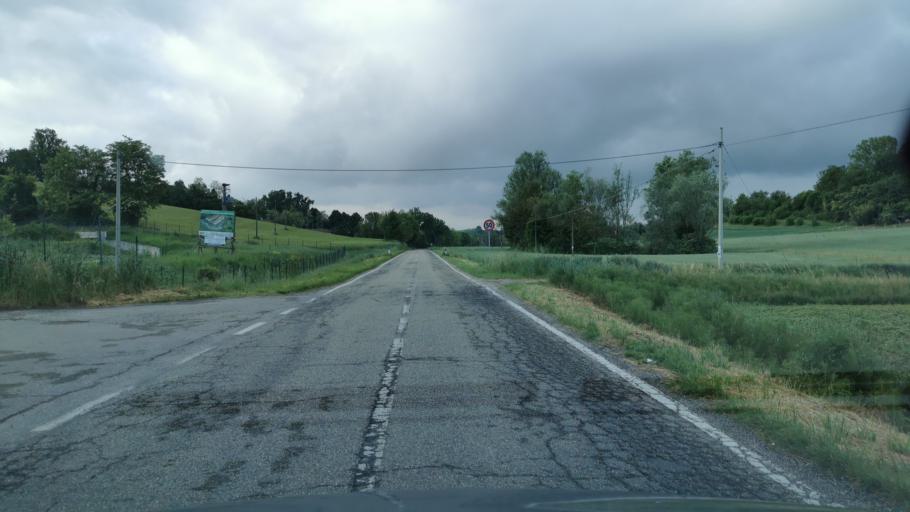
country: IT
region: Piedmont
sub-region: Provincia di Torino
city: Pino Torinese
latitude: 45.0071
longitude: 7.7824
